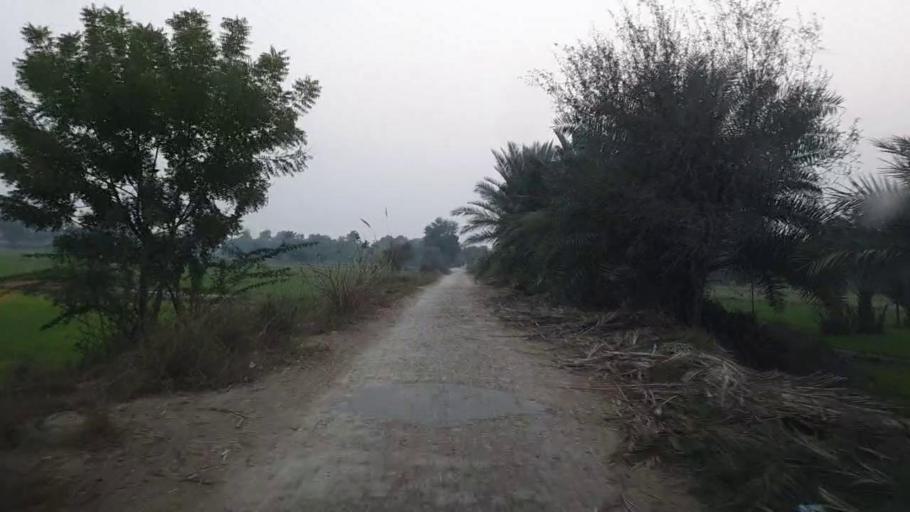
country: PK
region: Sindh
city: Kandiari
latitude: 26.9556
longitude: 68.4565
